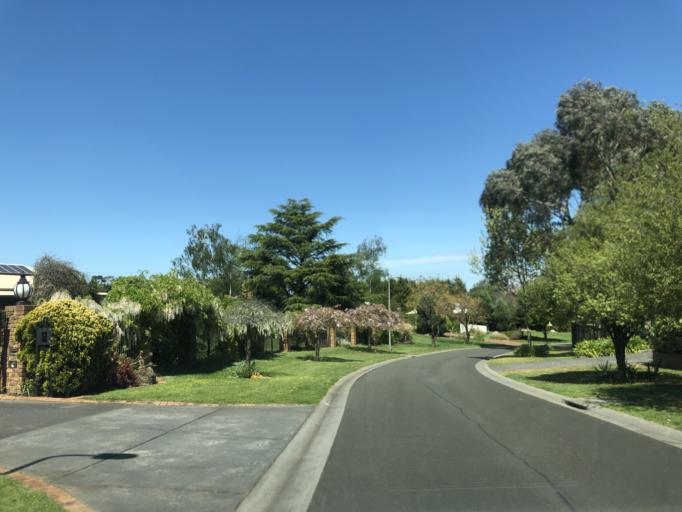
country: AU
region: Victoria
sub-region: Casey
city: Endeavour Hills
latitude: -37.9803
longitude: 145.2835
